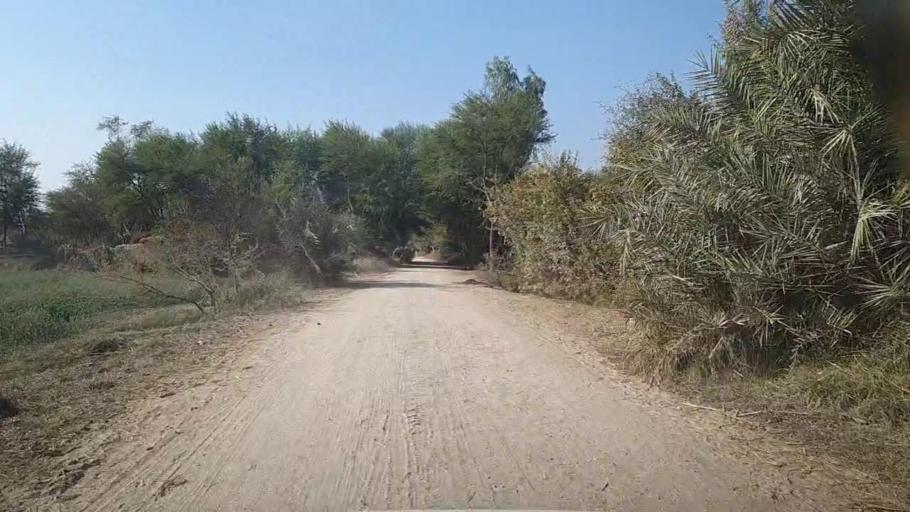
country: PK
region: Sindh
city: Mirpur Mathelo
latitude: 27.8964
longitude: 69.6526
